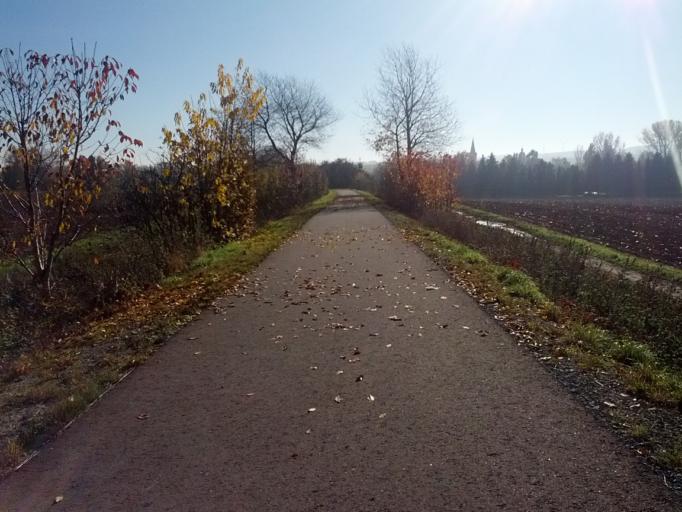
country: DE
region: Thuringia
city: Friedrichswerth
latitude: 50.9992
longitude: 10.5411
